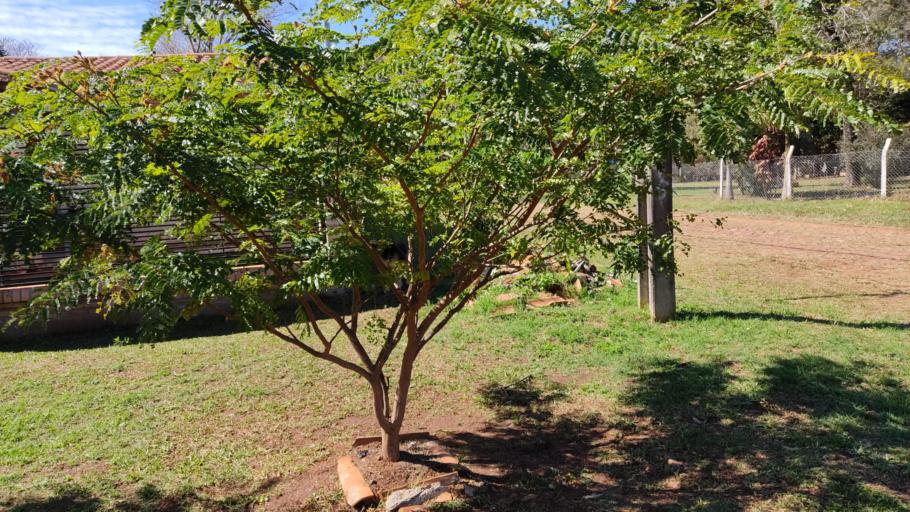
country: PY
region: Misiones
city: San Juan Bautista
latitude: -26.6769
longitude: -57.1424
